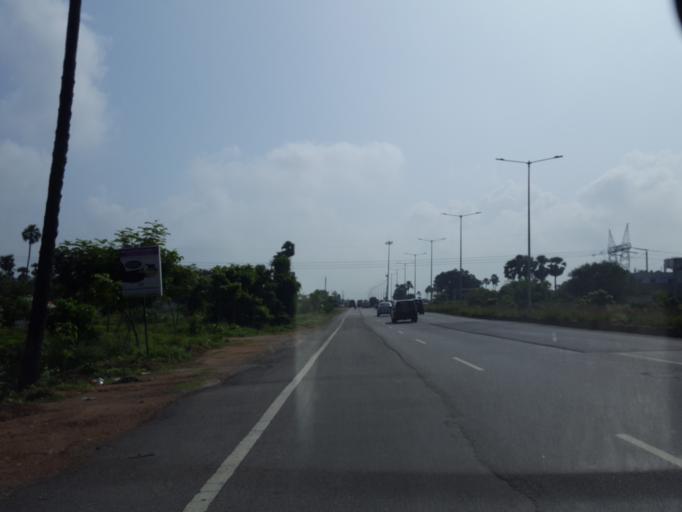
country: IN
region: Telangana
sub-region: Rangareddi
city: Ghatkesar
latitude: 17.3069
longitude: 78.7133
